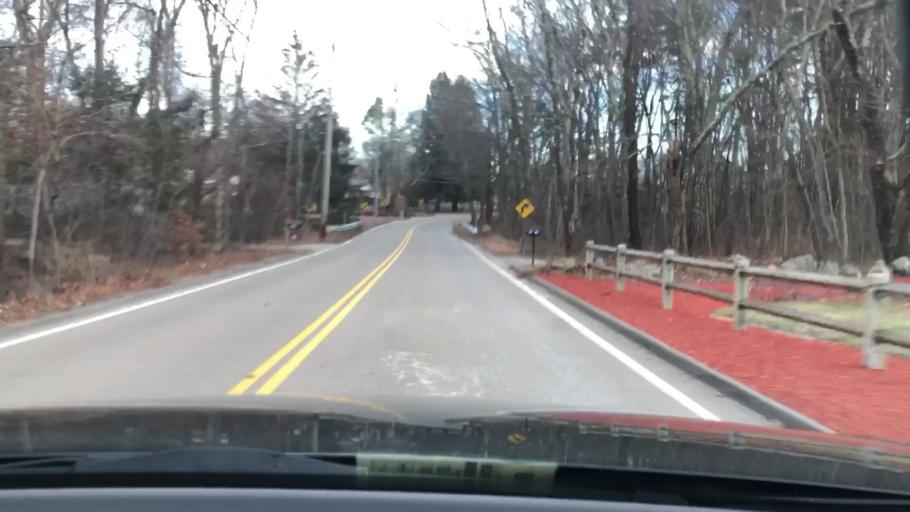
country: US
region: Massachusetts
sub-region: Worcester County
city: Blackstone
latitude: 42.0435
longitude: -71.5253
